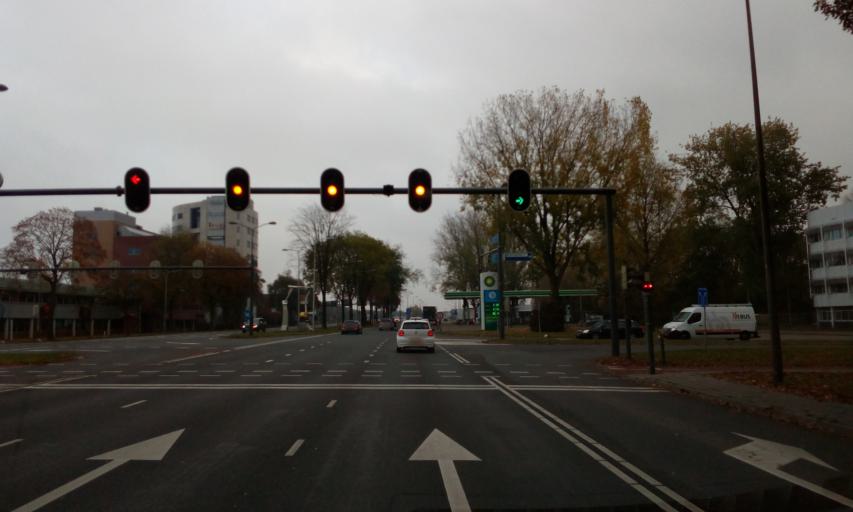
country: NL
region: Overijssel
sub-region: Gemeente Deventer
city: Deventer
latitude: 52.2394
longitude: 6.1763
